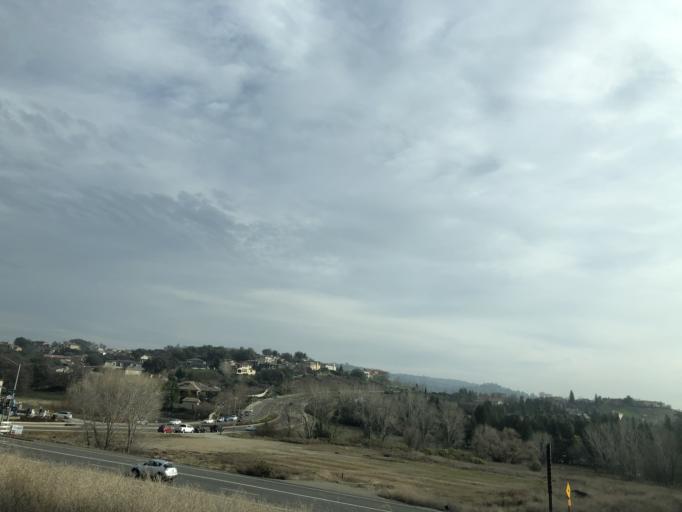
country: US
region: California
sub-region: El Dorado County
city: El Dorado Hills
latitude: 38.7014
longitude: -121.1080
